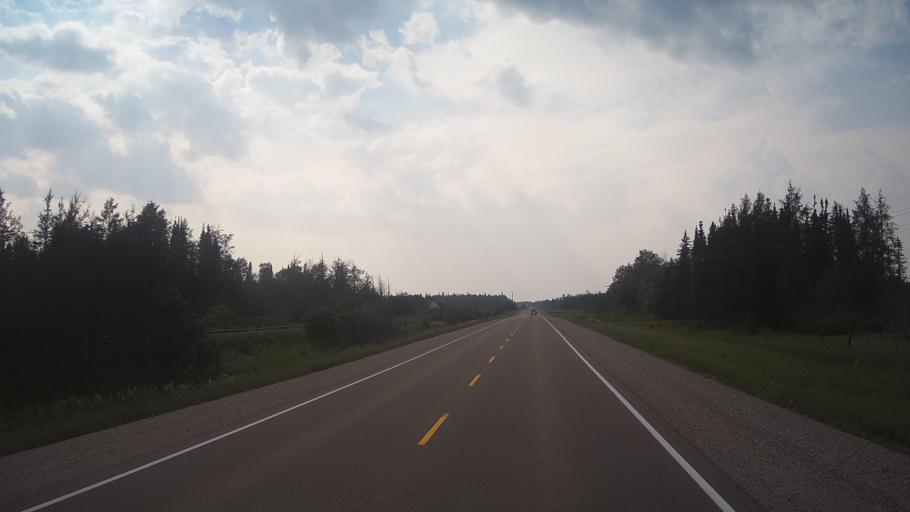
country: CA
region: Ontario
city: Kapuskasing
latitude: 49.5136
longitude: -82.7847
